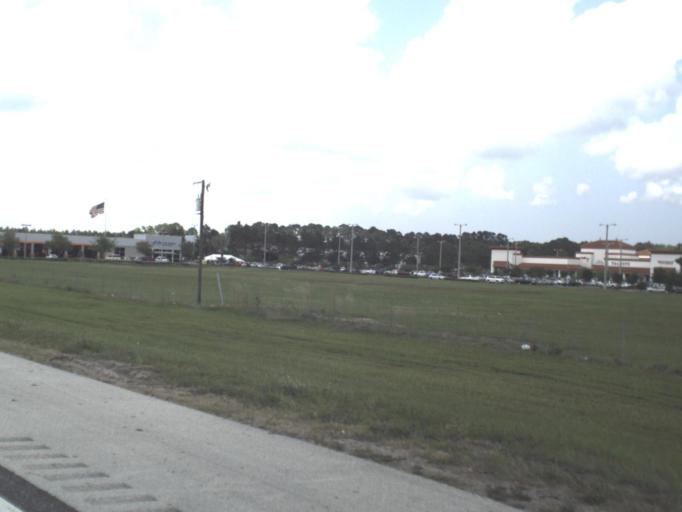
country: US
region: Florida
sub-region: Saint Johns County
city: Saint Augustine
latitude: 29.9241
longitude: -81.4148
